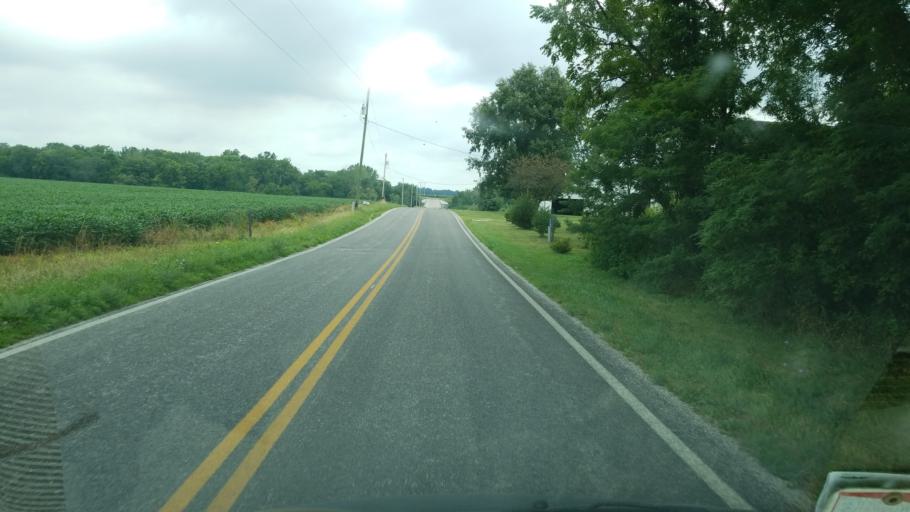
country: US
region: Ohio
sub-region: Seneca County
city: Tiffin
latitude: 41.2052
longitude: -83.1463
